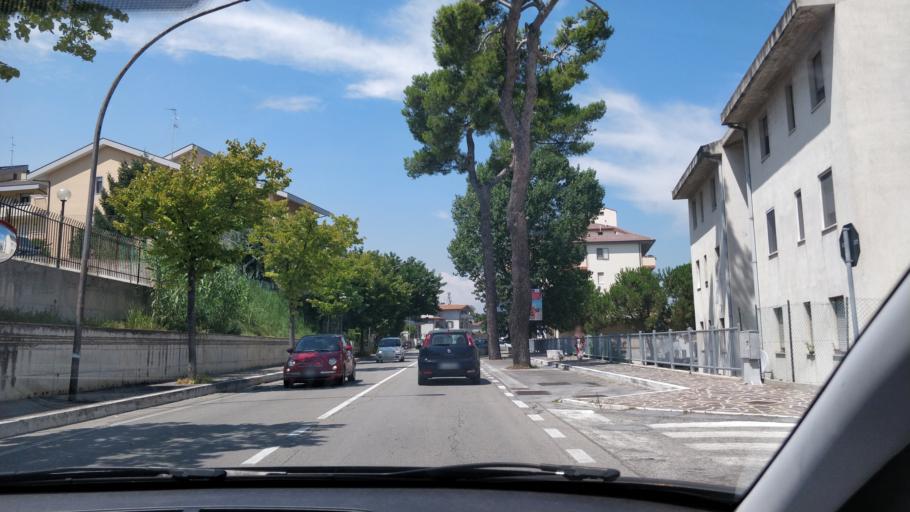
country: IT
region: Abruzzo
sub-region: Provincia di Chieti
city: Francavilla al Mare
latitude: 42.4078
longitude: 14.3085
